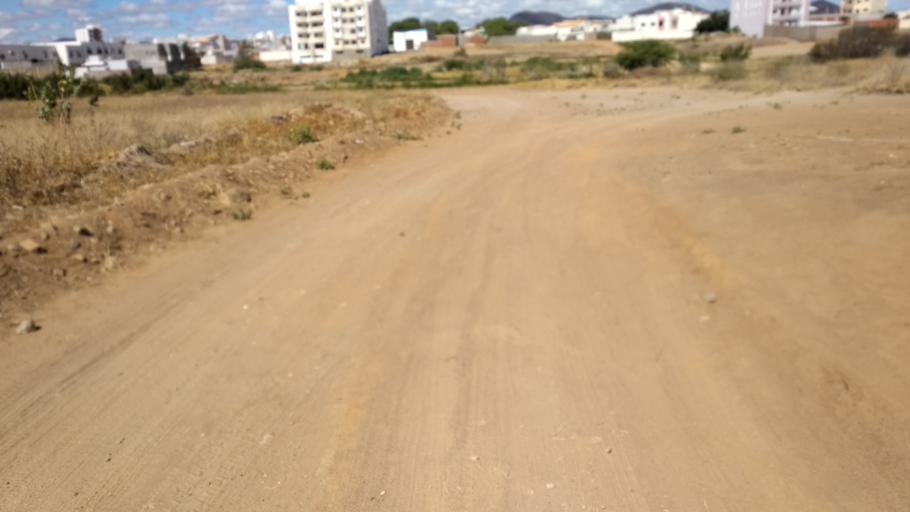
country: BR
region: Bahia
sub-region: Guanambi
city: Guanambi
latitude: -14.2305
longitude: -42.7731
